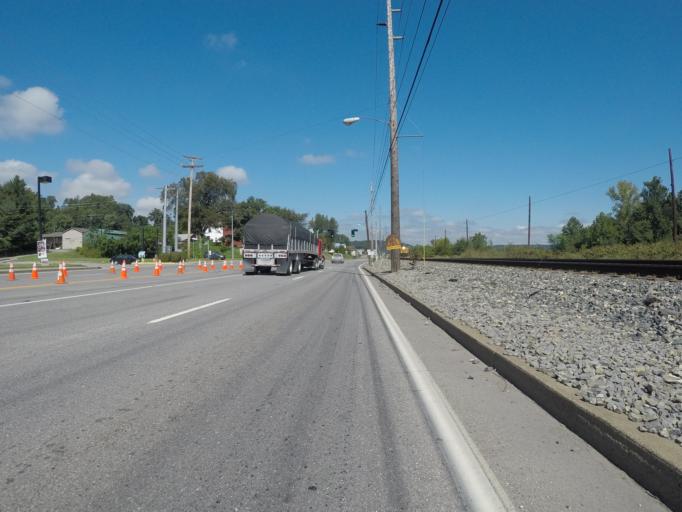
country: US
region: Ohio
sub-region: Lawrence County
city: South Point
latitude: 38.4389
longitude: -82.6086
